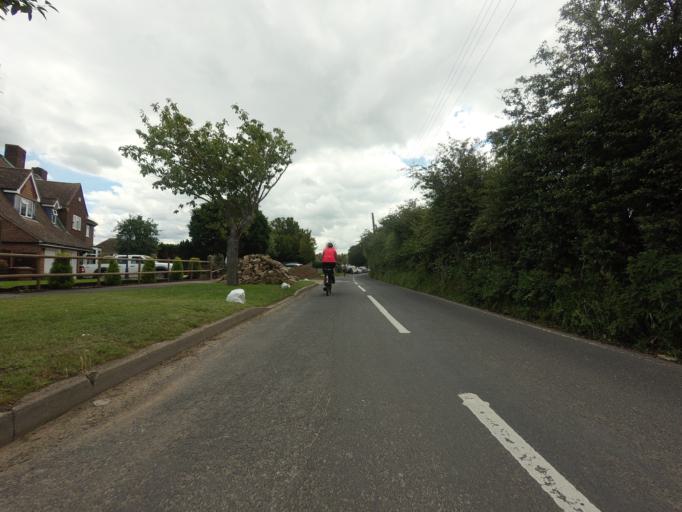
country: GB
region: England
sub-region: Medway
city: Allhallows
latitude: 51.4573
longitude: 0.6371
